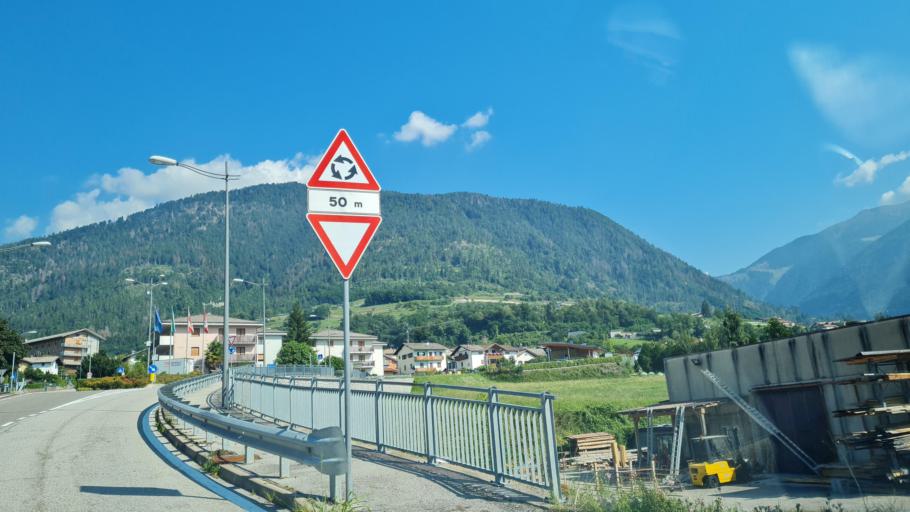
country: IT
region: Trentino-Alto Adige
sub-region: Provincia di Trento
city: Telve
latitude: 46.0672
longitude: 11.4823
